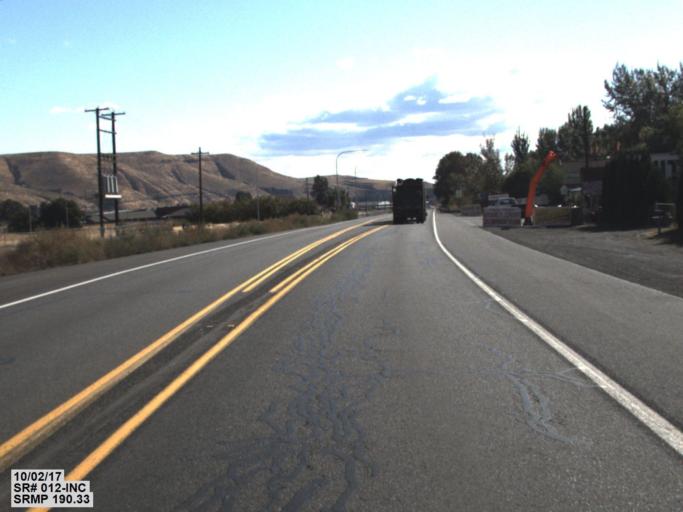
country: US
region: Washington
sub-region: Yakima County
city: Tieton
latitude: 46.7254
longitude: -120.6914
